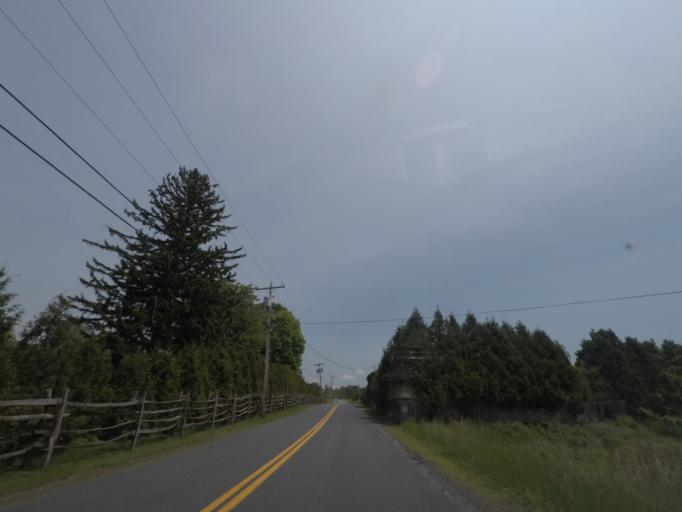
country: US
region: New York
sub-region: Columbia County
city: Niverville
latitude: 42.4755
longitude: -73.6947
